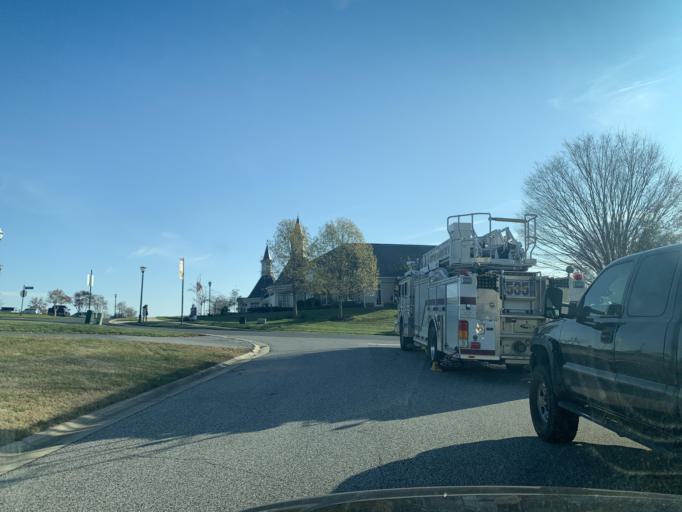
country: US
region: Maryland
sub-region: Harford County
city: Havre de Grace
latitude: 39.5538
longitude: -76.1290
